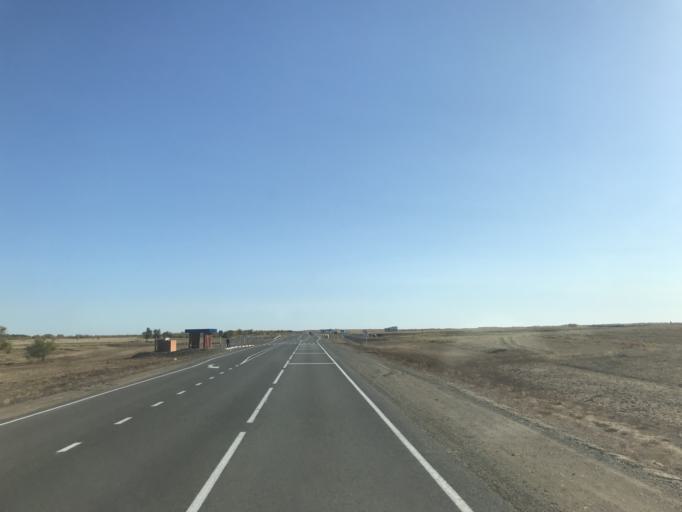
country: KZ
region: Pavlodar
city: Koktobe
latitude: 51.8171
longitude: 77.4690
